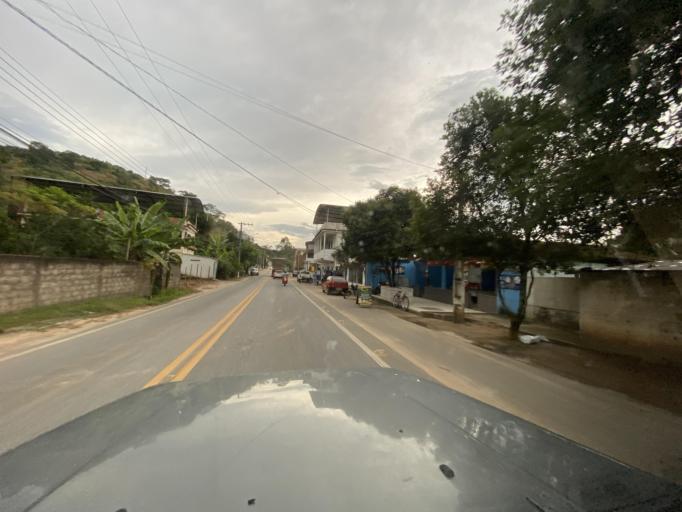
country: BR
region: Espirito Santo
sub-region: Jeronimo Monteiro
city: Jeronimo Monteiro
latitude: -20.7954
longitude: -41.3753
